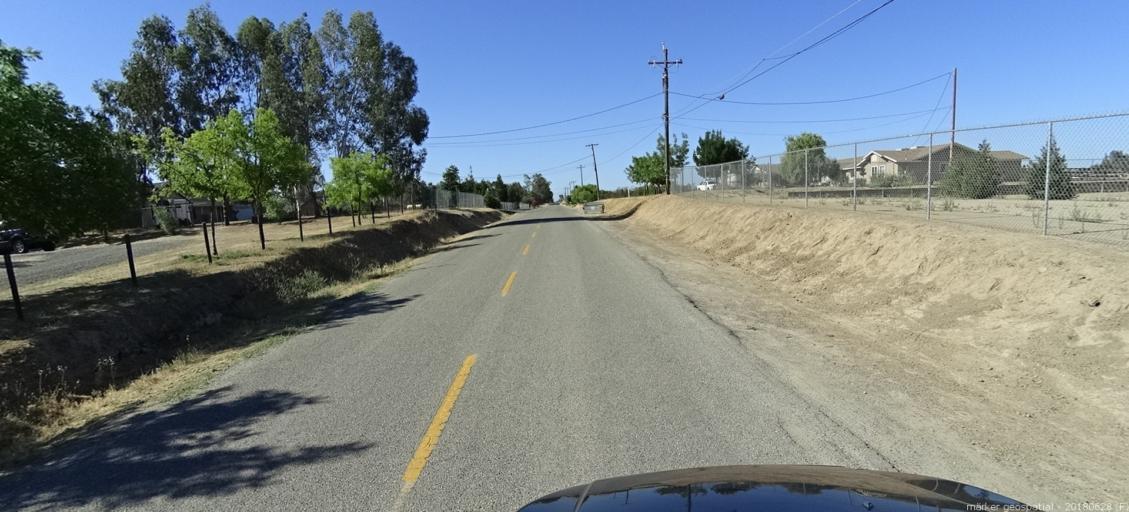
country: US
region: California
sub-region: Madera County
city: Bonadelle Ranchos-Madera Ranchos
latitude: 36.9999
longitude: -119.8865
